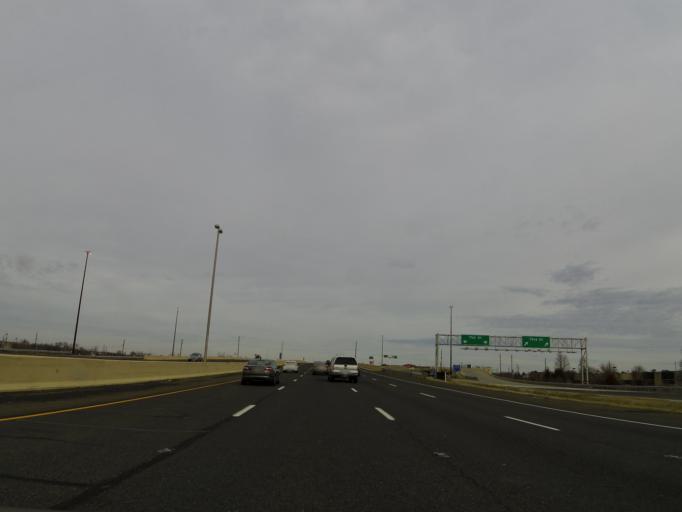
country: US
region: Indiana
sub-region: Boone County
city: Zionsville
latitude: 39.8781
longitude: -86.2689
